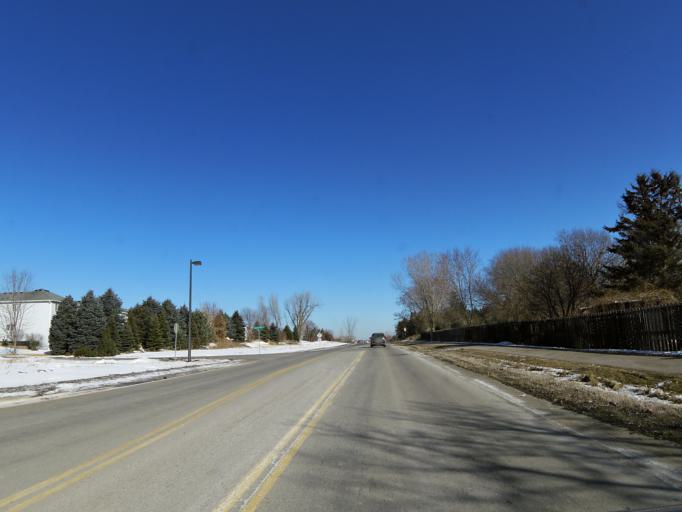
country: US
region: Minnesota
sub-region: Washington County
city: Woodbury
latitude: 44.9070
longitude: -92.9289
